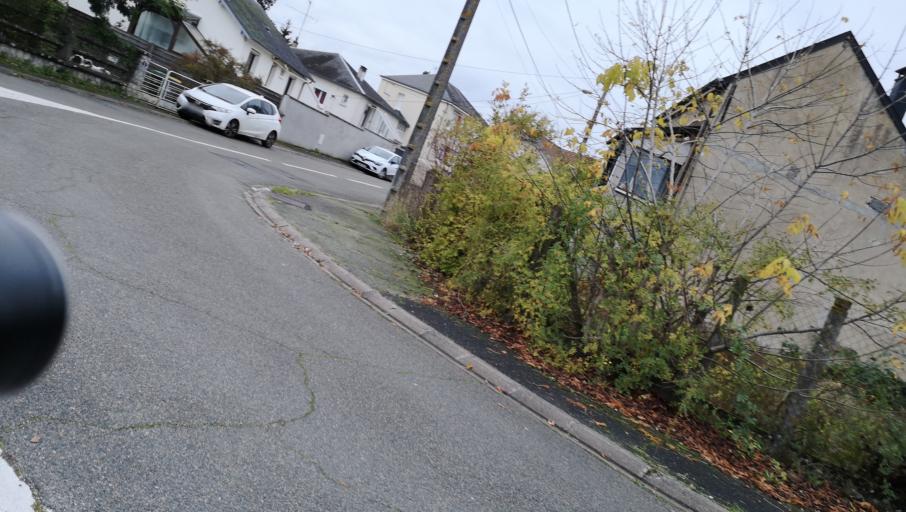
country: FR
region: Centre
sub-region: Departement du Loiret
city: Saint-Jean-de-Braye
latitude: 47.9052
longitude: 1.9525
